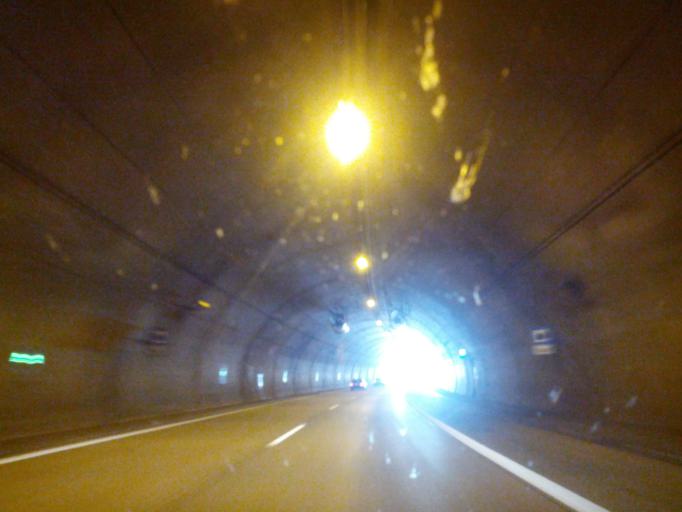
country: DE
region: Saxony
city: Freital
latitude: 51.0248
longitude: 13.6853
